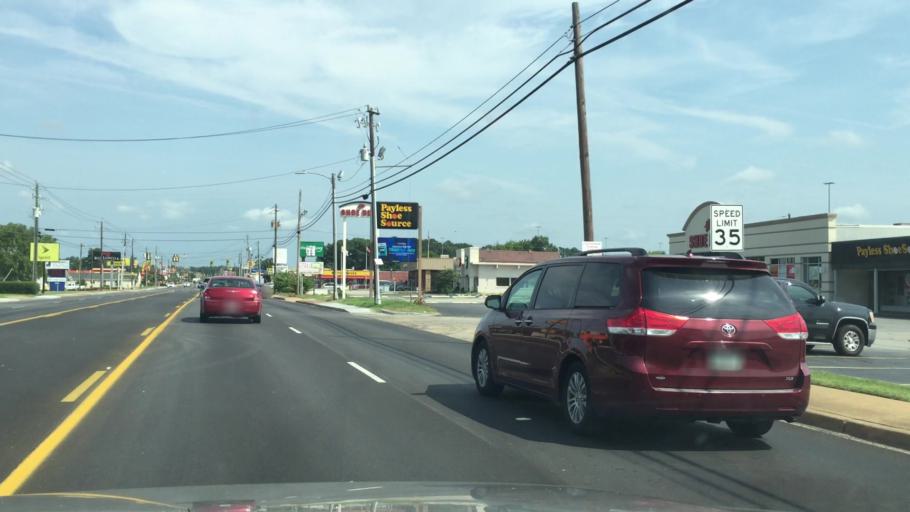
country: US
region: South Carolina
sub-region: Sumter County
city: Sumter
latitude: 33.9464
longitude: -80.3734
